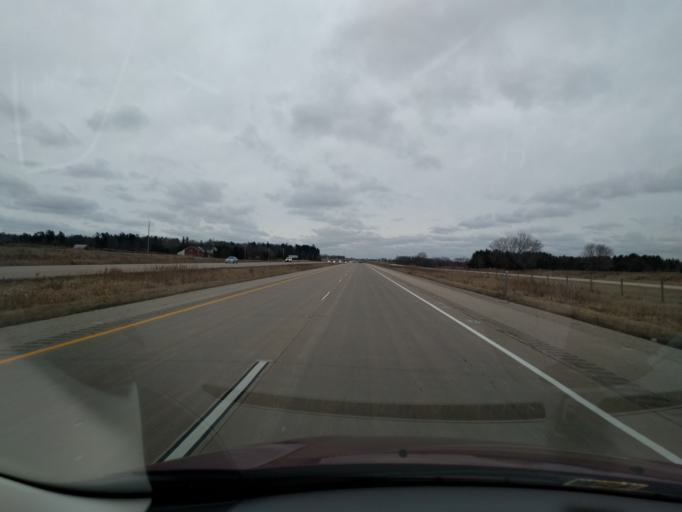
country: US
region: Wisconsin
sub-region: Winnebago County
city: Winneconne
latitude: 44.2340
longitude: -88.7584
